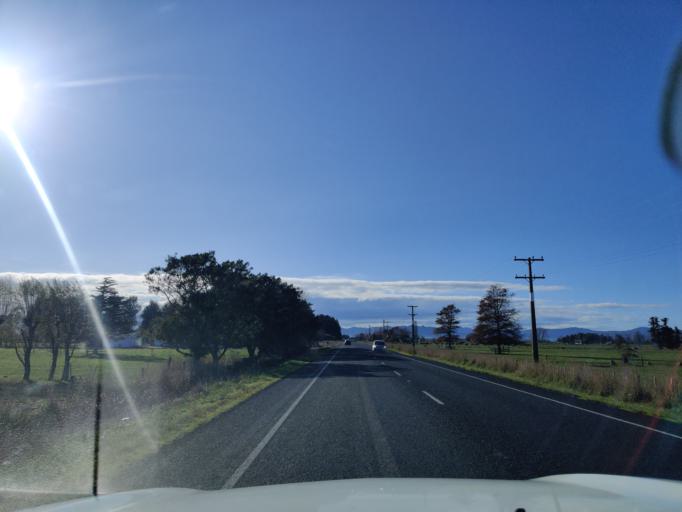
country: NZ
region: Waikato
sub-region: Hauraki District
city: Ngatea
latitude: -37.2732
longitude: 175.5157
